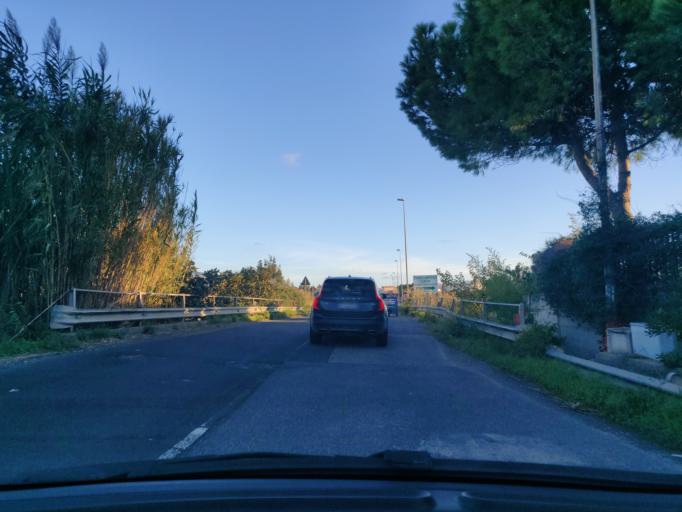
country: IT
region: Latium
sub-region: Citta metropolitana di Roma Capitale
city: Civitavecchia
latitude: 42.1116
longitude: 11.7767
